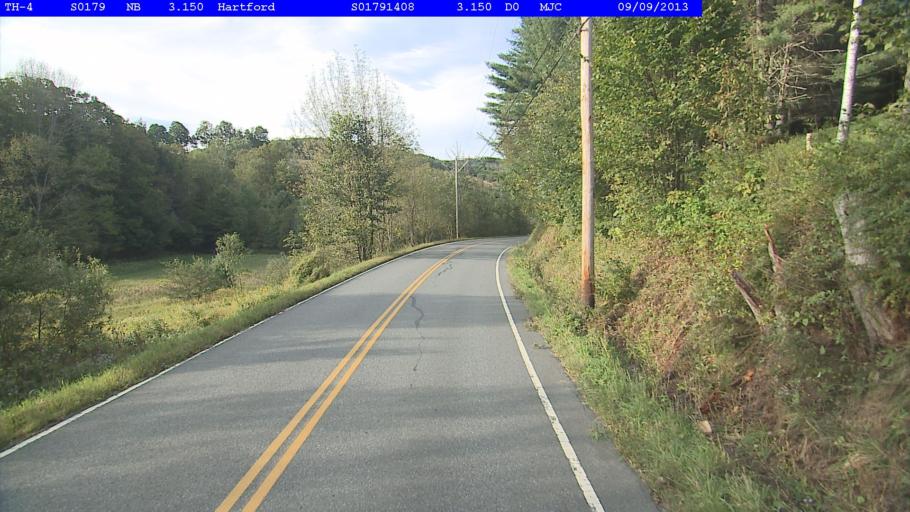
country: US
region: Vermont
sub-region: Windsor County
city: Woodstock
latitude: 43.6860
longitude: -72.4449
